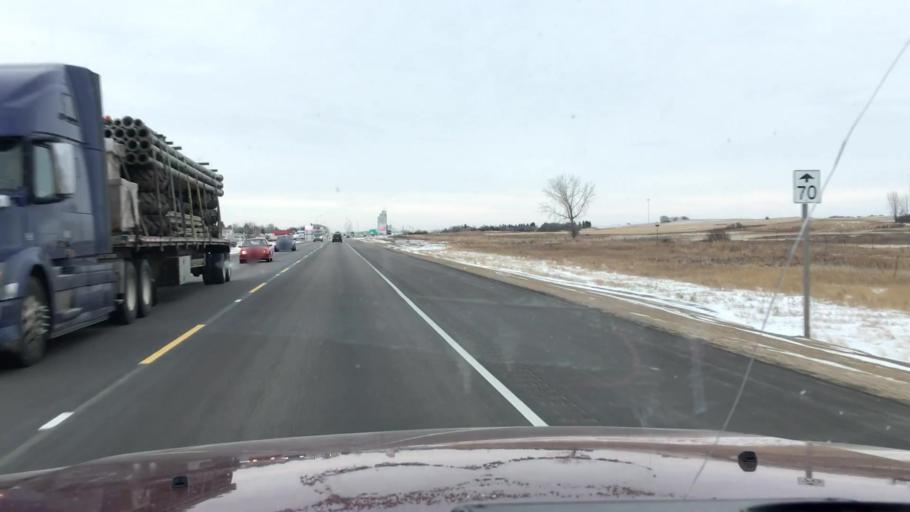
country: CA
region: Saskatchewan
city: Moose Jaw
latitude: 50.8559
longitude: -105.5778
